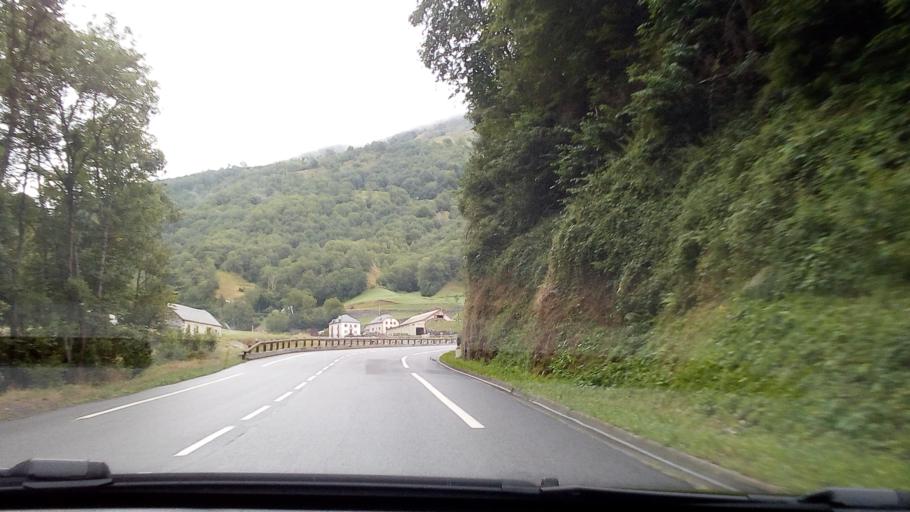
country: FR
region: Midi-Pyrenees
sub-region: Departement des Hautes-Pyrenees
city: Luz-Saint-Sauveur
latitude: 42.8830
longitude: 0.0336
